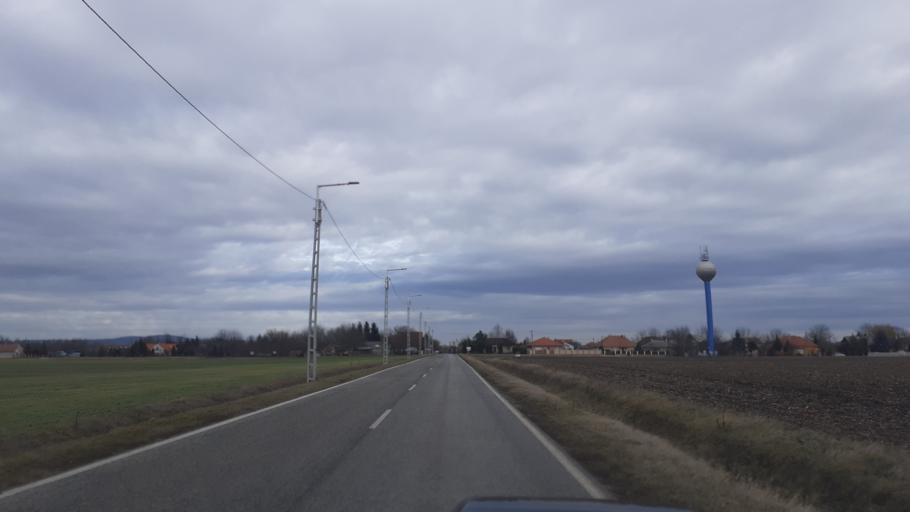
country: HU
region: Fejer
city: Pakozd
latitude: 47.1637
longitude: 18.5147
